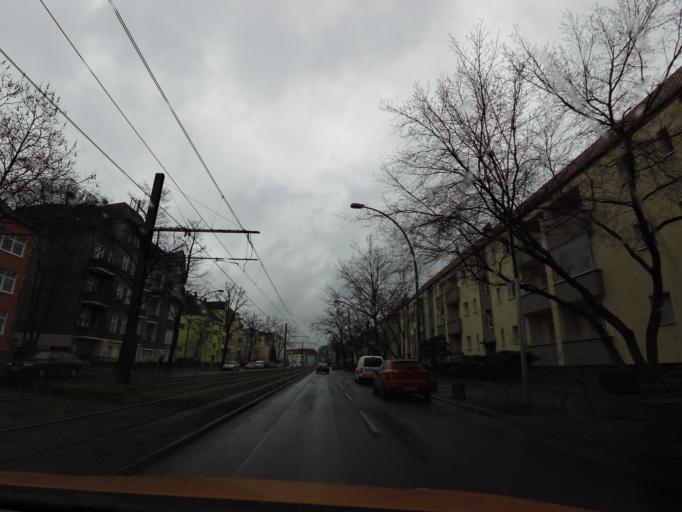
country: DE
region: Berlin
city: Karlshorst
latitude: 52.4880
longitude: 13.5274
